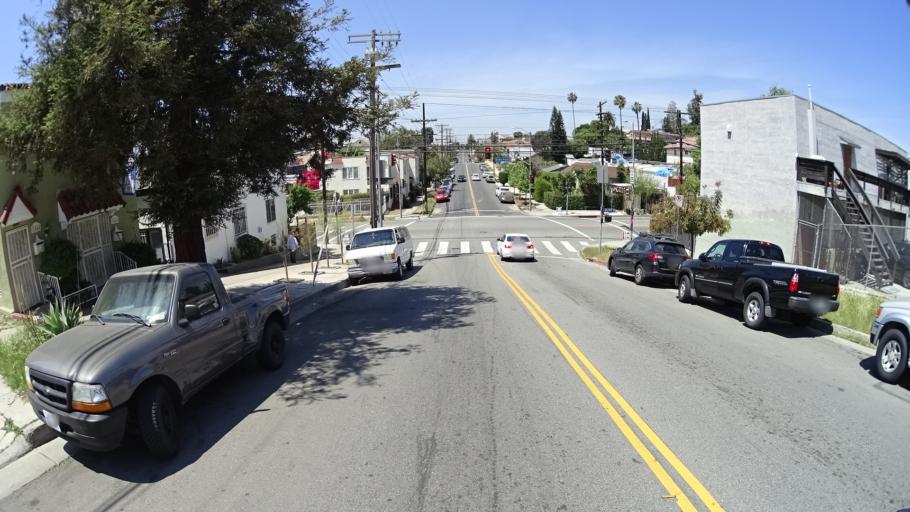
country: US
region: California
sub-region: Los Angeles County
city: Echo Park
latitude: 34.0797
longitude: -118.2551
